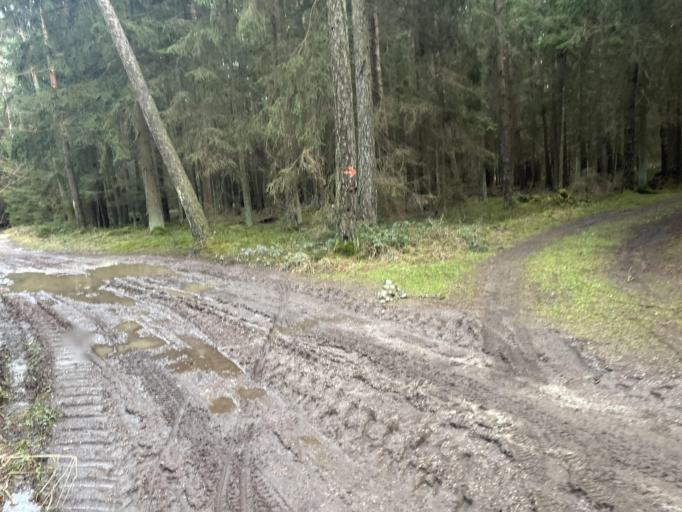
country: DE
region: Bavaria
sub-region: Lower Bavaria
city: Biburg
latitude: 48.8265
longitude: 11.9091
